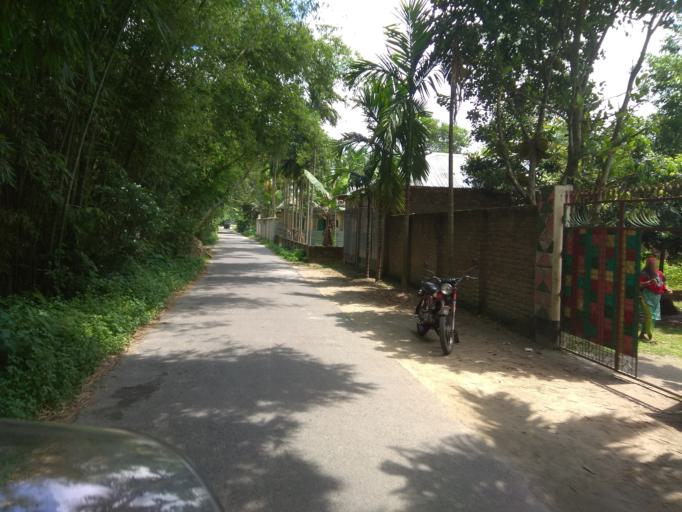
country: IN
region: West Bengal
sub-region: Koch Bihar
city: Haldibari
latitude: 26.1633
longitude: 88.9241
